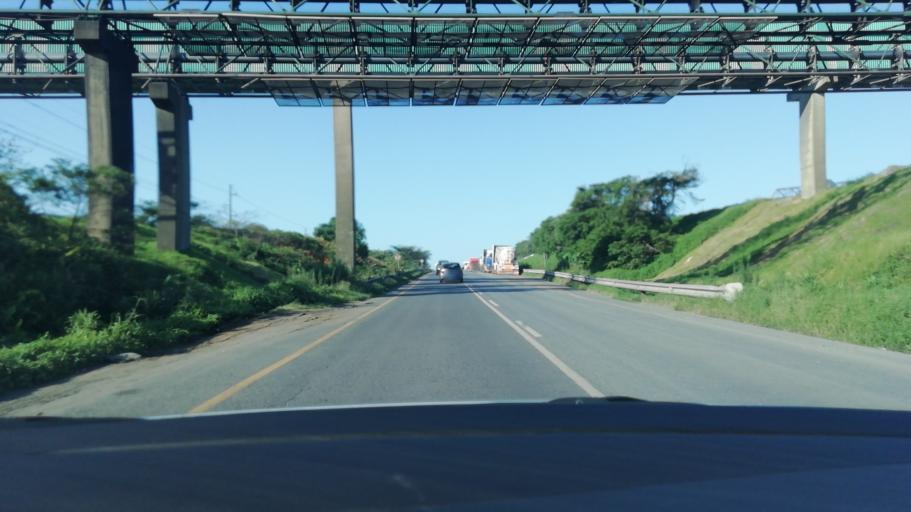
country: ZA
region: KwaZulu-Natal
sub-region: uThungulu District Municipality
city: Richards Bay
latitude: -28.7783
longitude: 32.0299
